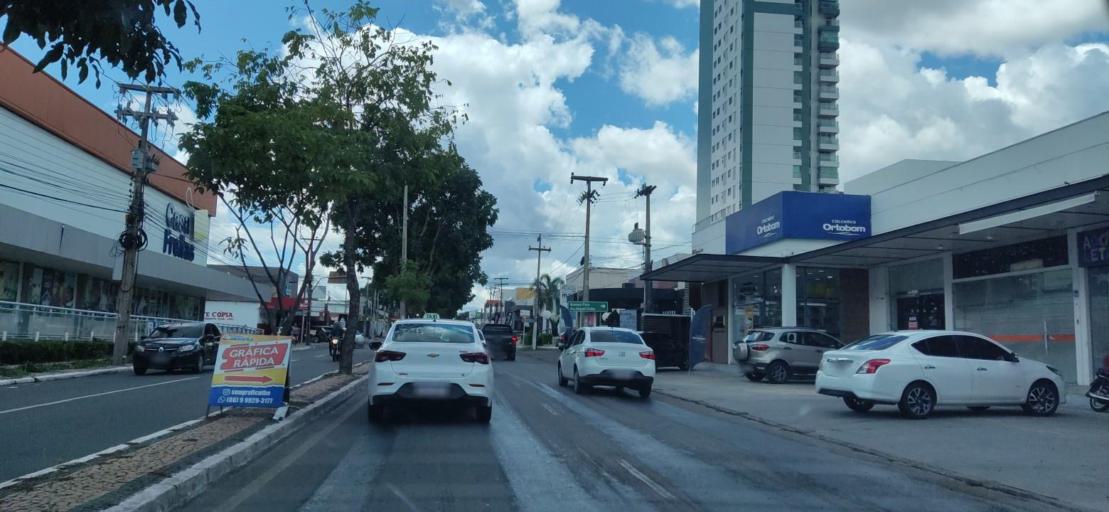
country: BR
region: Piaui
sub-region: Teresina
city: Teresina
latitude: -5.0760
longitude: -42.7908
